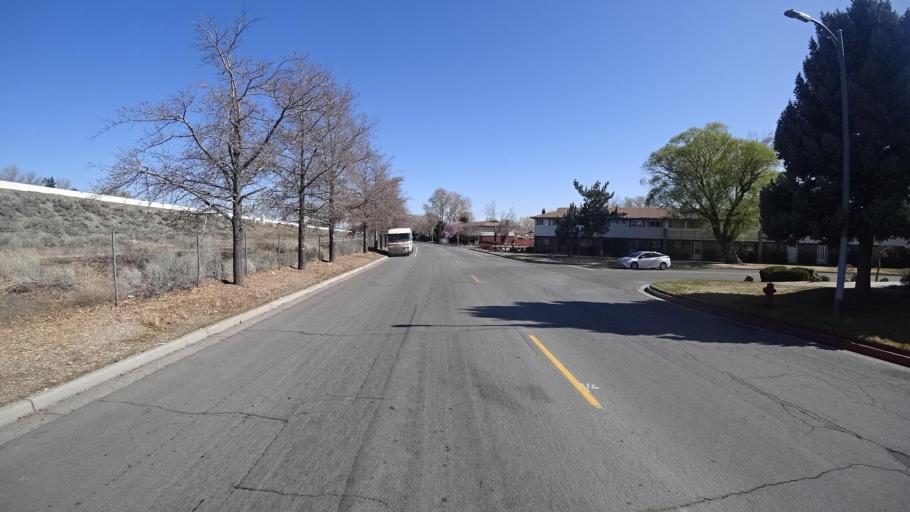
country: US
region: Nevada
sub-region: Washoe County
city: Reno
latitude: 39.4809
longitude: -119.7872
